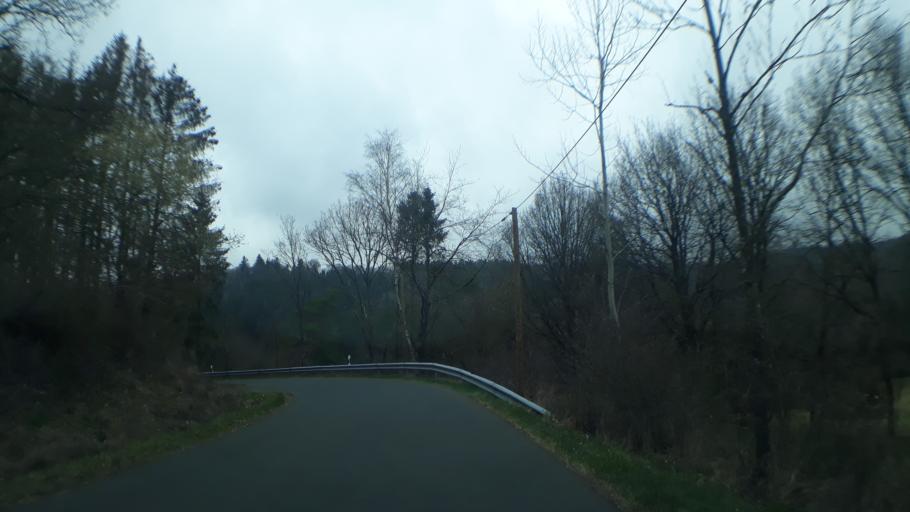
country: DE
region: North Rhine-Westphalia
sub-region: Regierungsbezirk Koln
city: Schleiden
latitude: 50.5399
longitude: 6.5034
